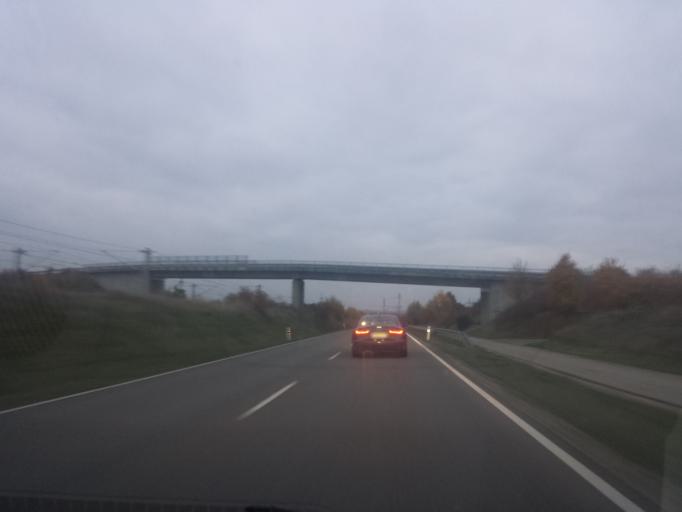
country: DE
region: Bavaria
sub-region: Upper Bavaria
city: Wettstetten
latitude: 48.8059
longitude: 11.4271
